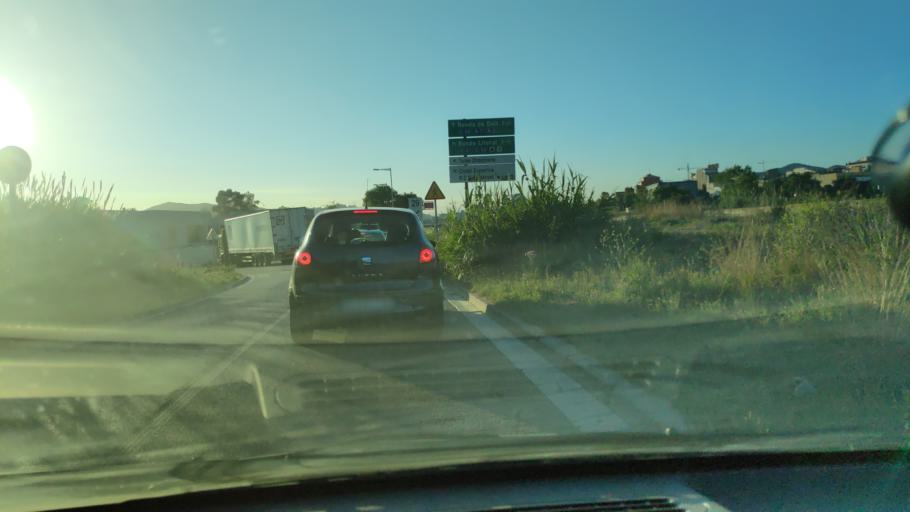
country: ES
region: Catalonia
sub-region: Provincia de Barcelona
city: Sant Adria de Besos
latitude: 41.4280
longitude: 2.2162
